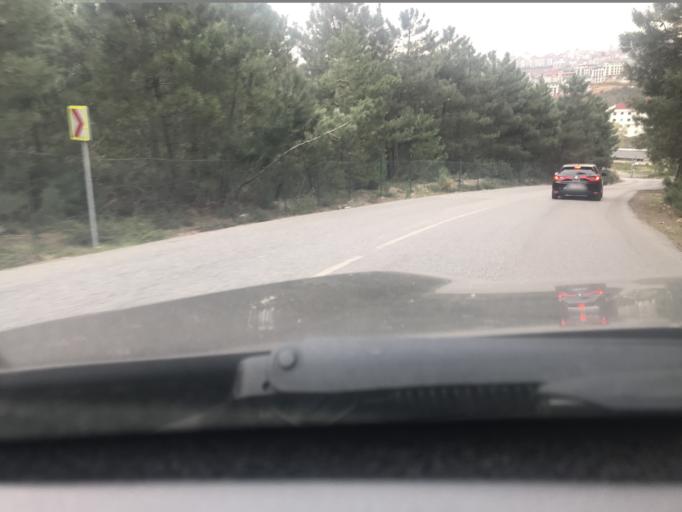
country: TR
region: Istanbul
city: Umraniye
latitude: 41.0416
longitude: 29.1707
